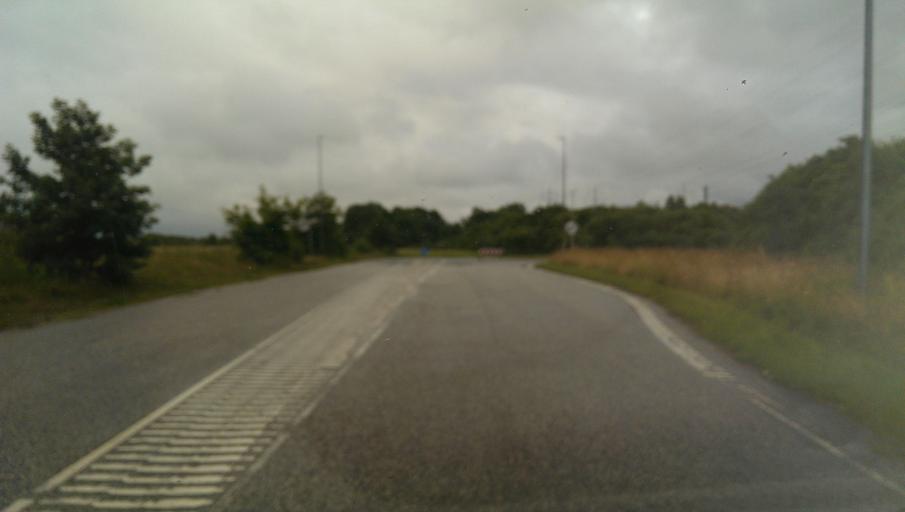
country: DK
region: South Denmark
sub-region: Esbjerg Kommune
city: Esbjerg
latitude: 55.4940
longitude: 8.5013
